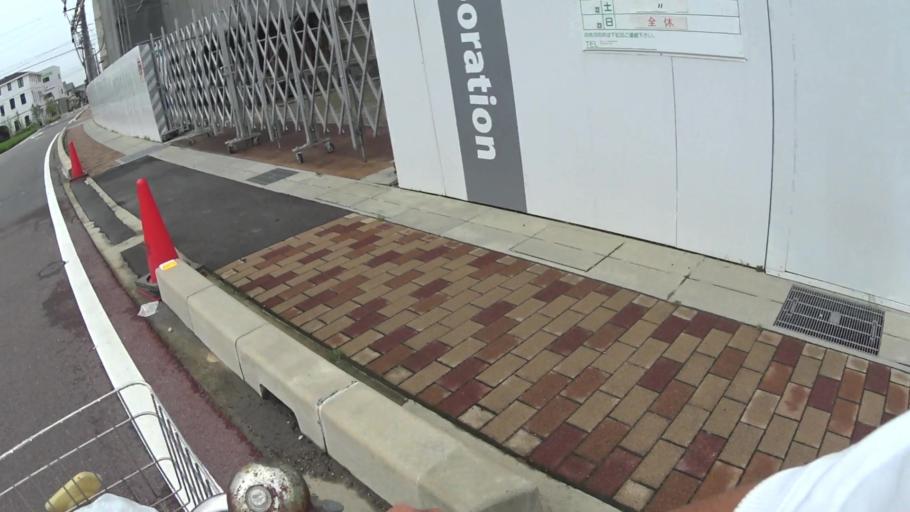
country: JP
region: Kyoto
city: Muko
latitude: 34.9595
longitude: 135.7064
